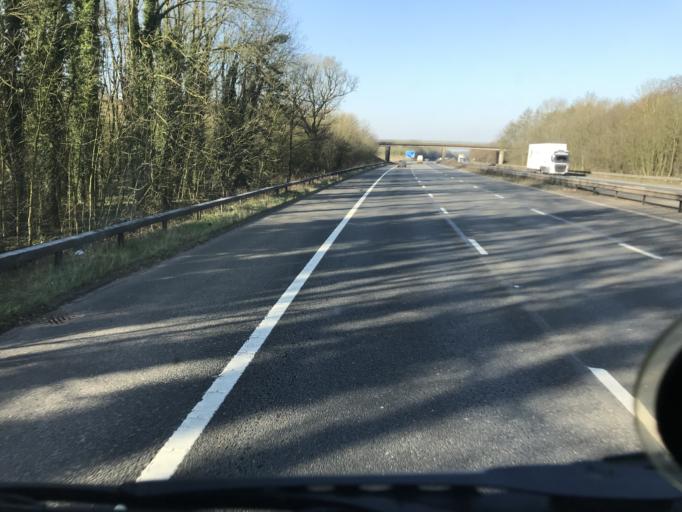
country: GB
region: England
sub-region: Borough of Halton
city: Daresbury
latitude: 53.3295
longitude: -2.6191
